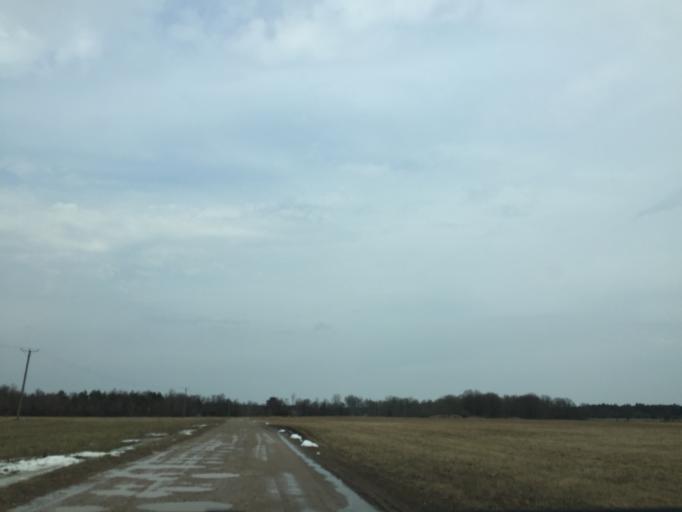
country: EE
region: Saare
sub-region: Kuressaare linn
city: Kuressaare
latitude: 58.4352
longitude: 22.1434
